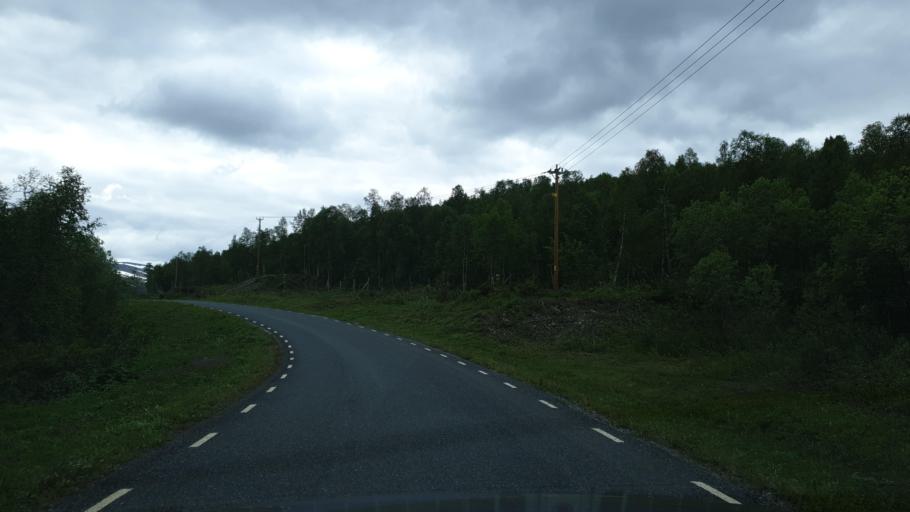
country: NO
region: Nordland
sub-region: Hattfjelldal
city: Hattfjelldal
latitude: 65.4175
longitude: 14.7379
